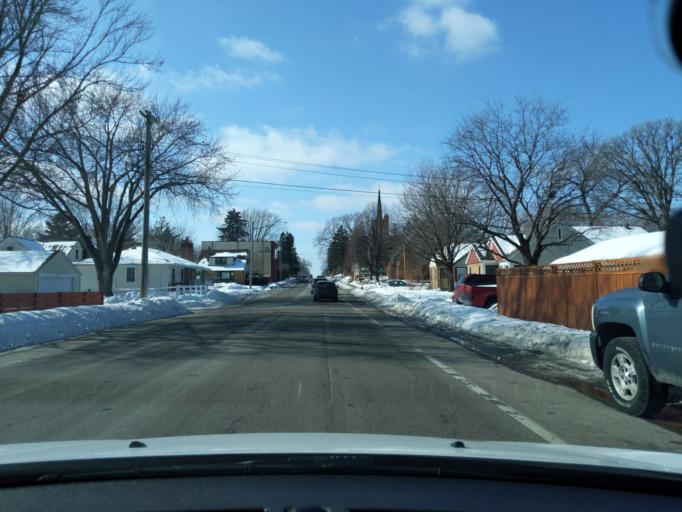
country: US
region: Minnesota
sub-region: Hennepin County
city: Saint Anthony
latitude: 45.0133
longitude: -93.2296
